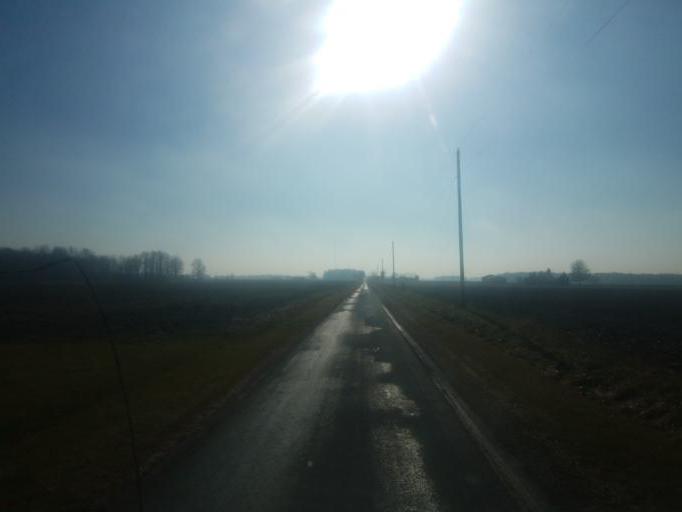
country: US
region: Ohio
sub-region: Seneca County
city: Tiffin
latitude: 40.9703
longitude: -83.0744
